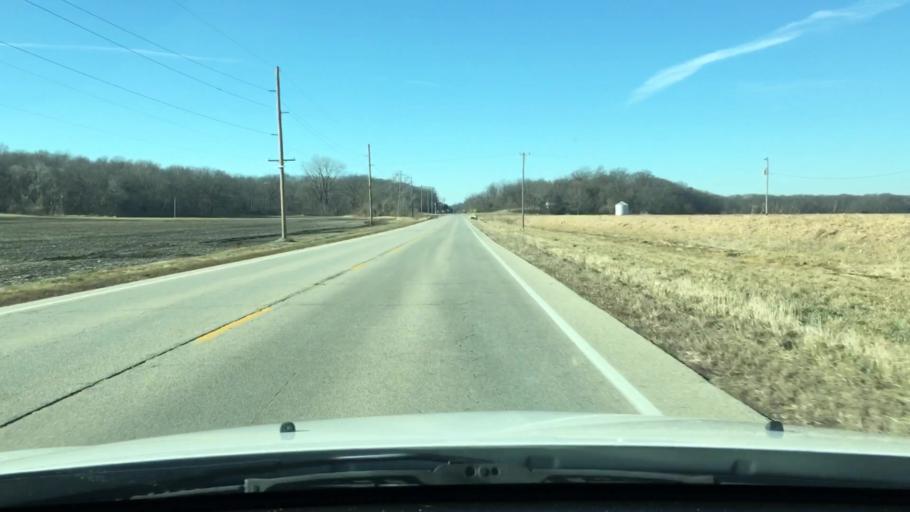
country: US
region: Illinois
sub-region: Mason County
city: Havana
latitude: 40.3041
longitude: -90.1327
